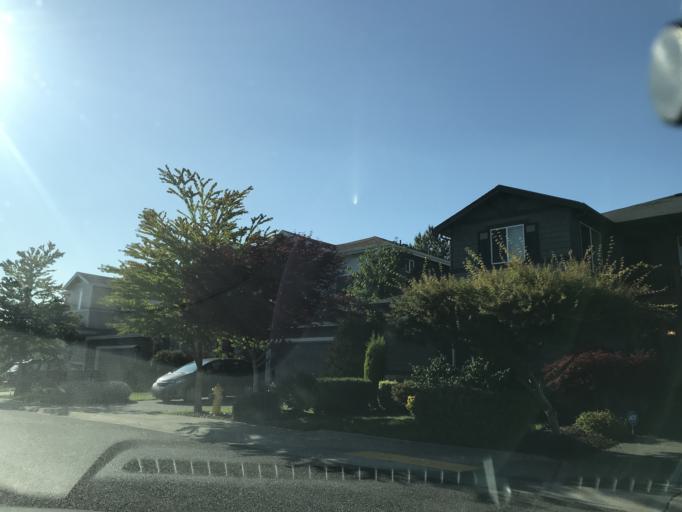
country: US
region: Washington
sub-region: King County
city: Ravensdale
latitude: 47.3557
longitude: -122.0003
